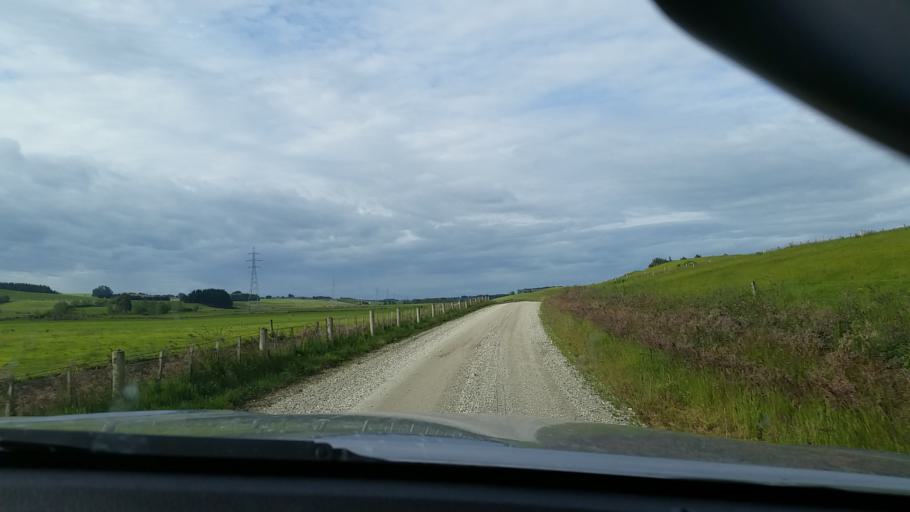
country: NZ
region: Southland
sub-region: Gore District
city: Gore
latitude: -46.2091
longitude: 168.7612
